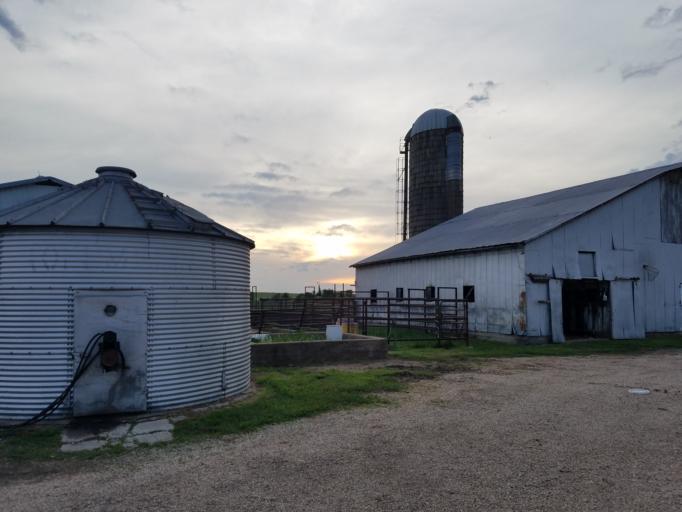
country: US
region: Oklahoma
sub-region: Mayes County
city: Chouteau
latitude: 36.1379
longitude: -95.3875
